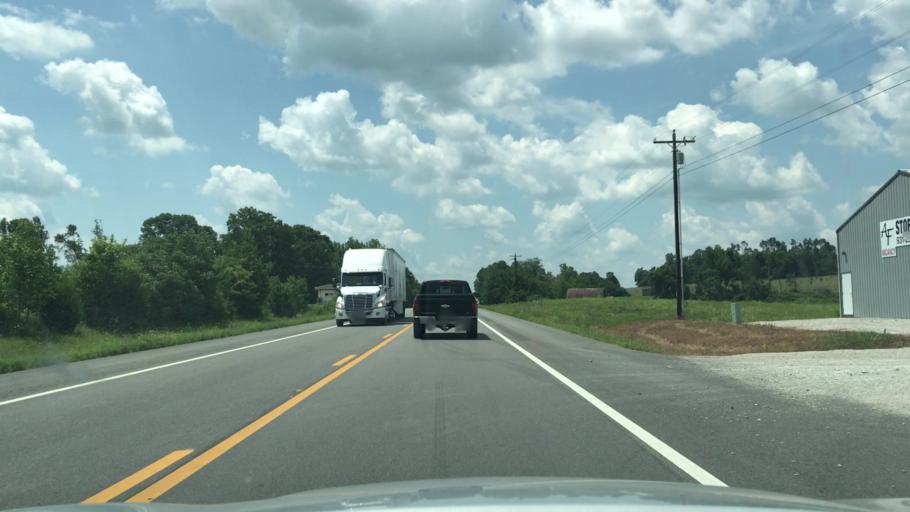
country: US
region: Tennessee
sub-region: Pickett County
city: Byrdstown
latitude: 36.5109
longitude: -85.1723
